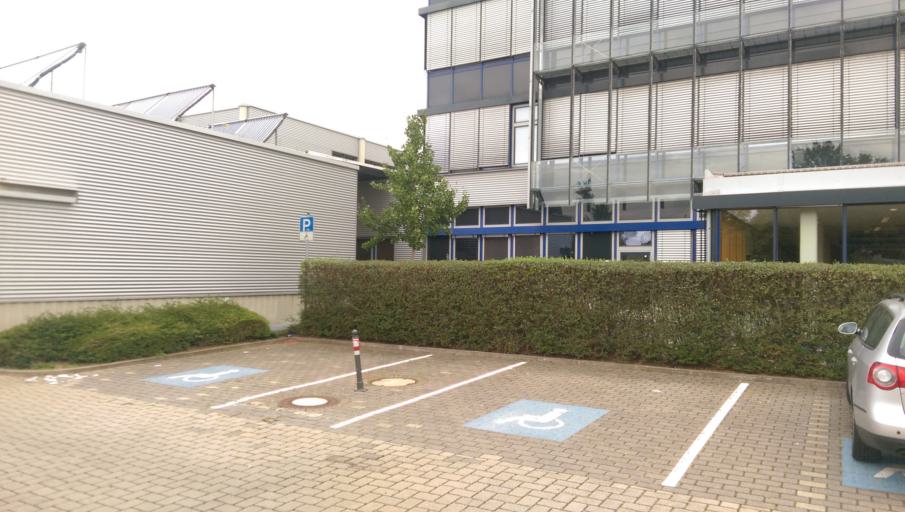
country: DE
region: North Rhine-Westphalia
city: Sankt Augustin
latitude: 50.7796
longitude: 7.1820
